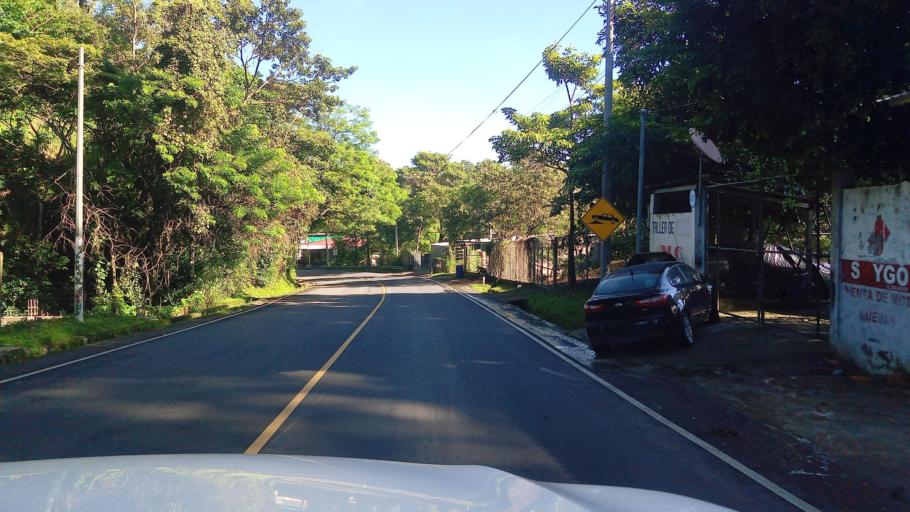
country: HN
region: Ocotepeque
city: Antigua Ocotepeque
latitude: 14.3206
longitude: -89.1760
